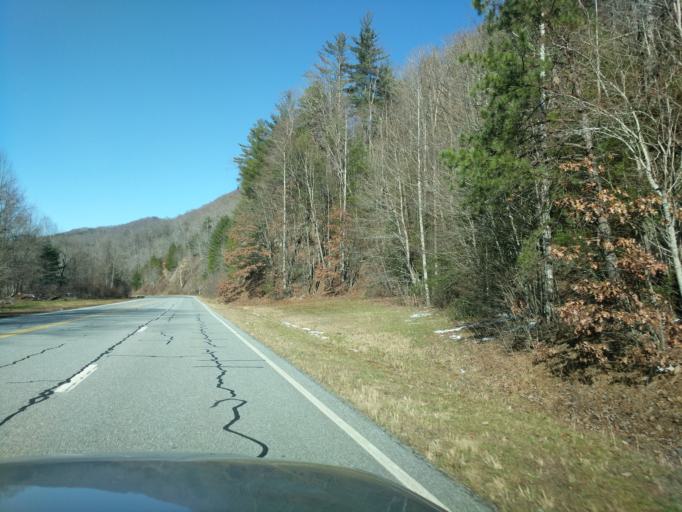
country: US
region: Georgia
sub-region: Towns County
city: Hiawassee
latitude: 34.8974
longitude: -83.6070
